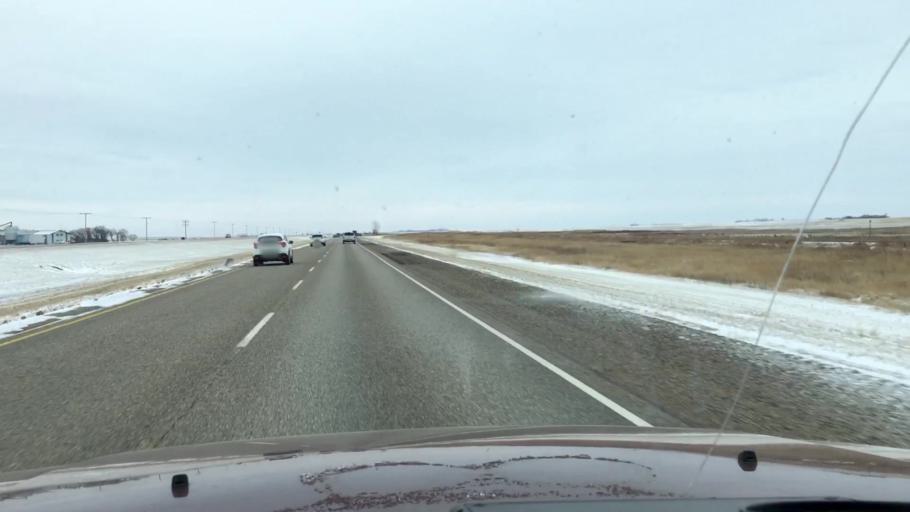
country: CA
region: Saskatchewan
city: Moose Jaw
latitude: 51.0121
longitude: -105.7772
